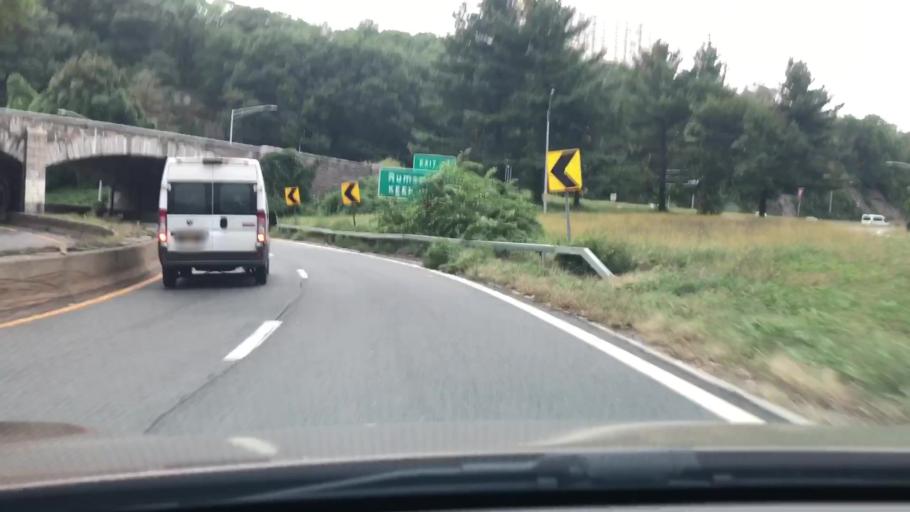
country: US
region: New York
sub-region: Westchester County
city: Yonkers
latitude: 40.9325
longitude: -73.8782
